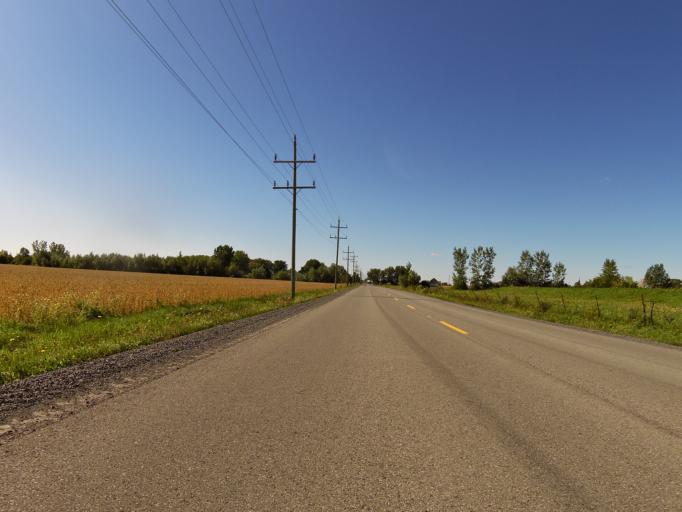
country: CA
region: Ontario
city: Casselman
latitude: 45.2697
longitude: -75.2472
